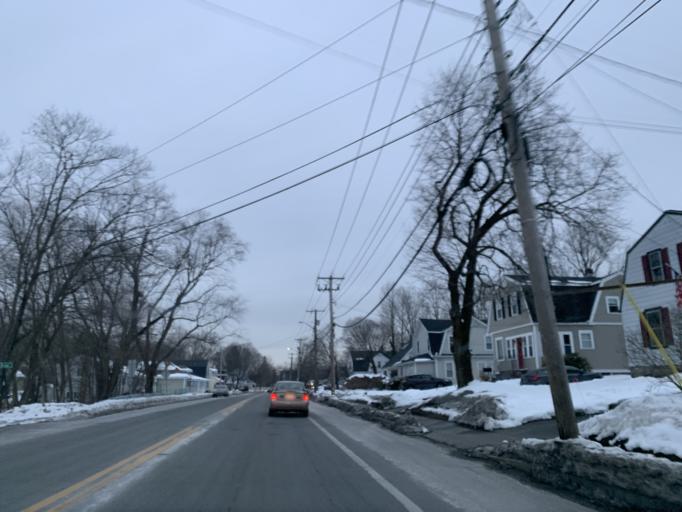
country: US
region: Massachusetts
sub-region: Norfolk County
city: Stoughton
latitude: 42.1201
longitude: -71.0878
